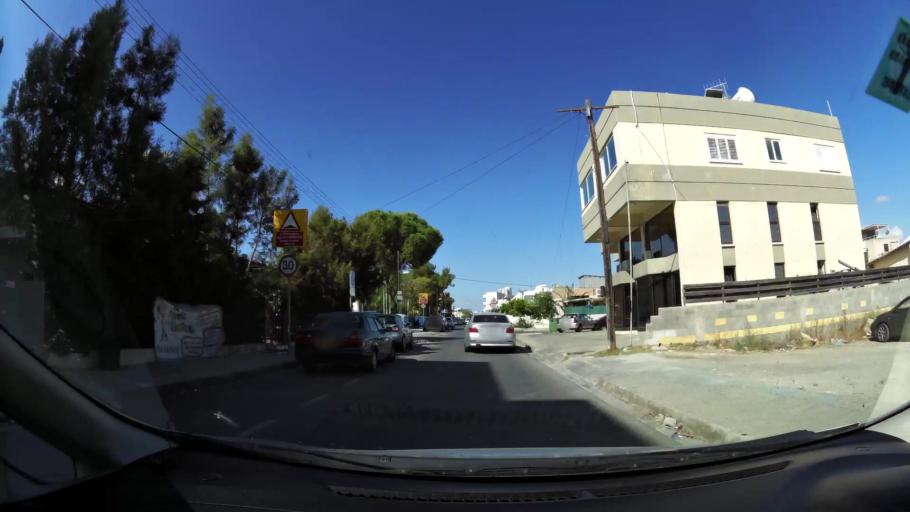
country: CY
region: Lefkosia
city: Nicosia
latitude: 35.1380
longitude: 33.3412
